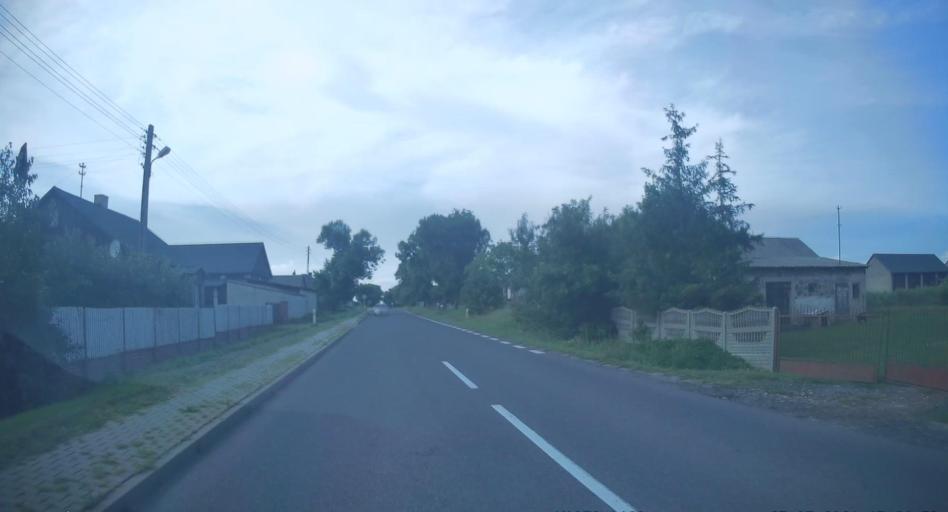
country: PL
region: Lodz Voivodeship
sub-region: Powiat tomaszowski
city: Rzeczyca
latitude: 51.6297
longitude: 20.2917
